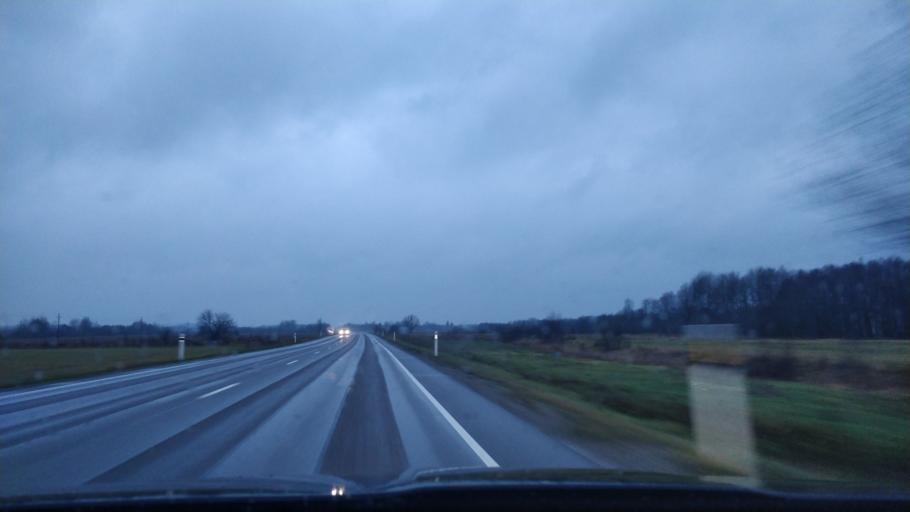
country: EE
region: Laeaene
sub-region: Lihula vald
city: Lihula
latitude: 58.7178
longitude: 23.8915
